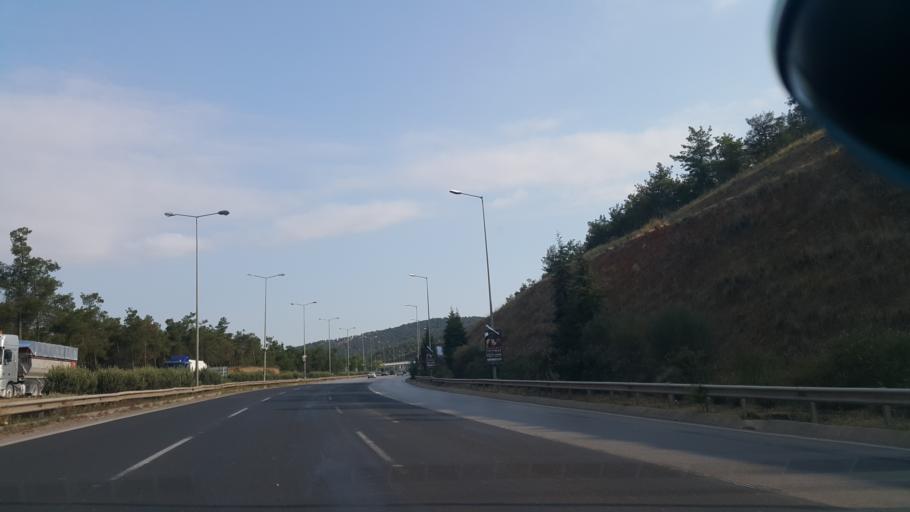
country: GR
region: Central Macedonia
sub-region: Nomos Thessalonikis
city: Triandria
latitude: 40.6174
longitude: 22.9839
